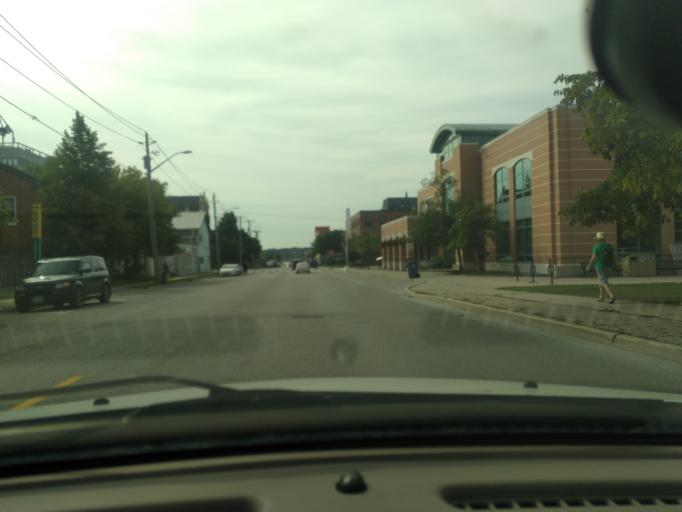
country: CA
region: Ontario
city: Barrie
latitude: 44.3924
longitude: -79.6880
